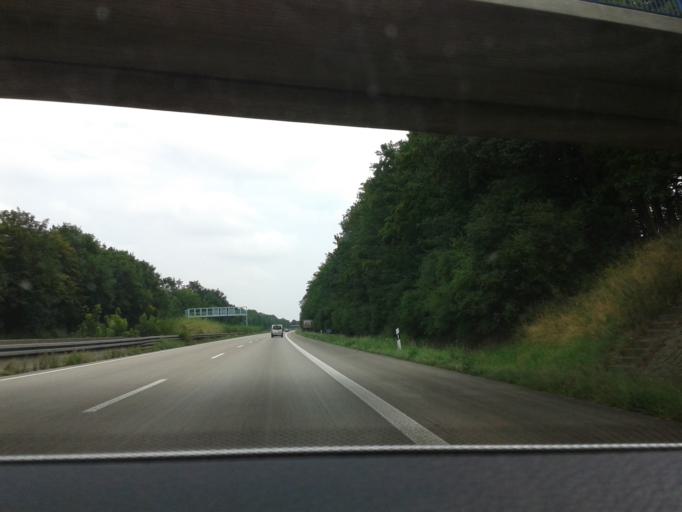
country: DE
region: North Rhine-Westphalia
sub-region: Regierungsbezirk Arnsberg
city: Soest
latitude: 51.5466
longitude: 8.0660
